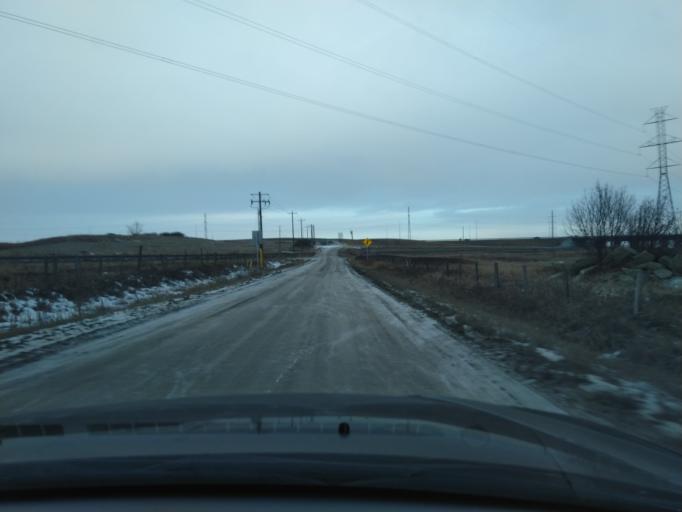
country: CA
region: Alberta
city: Airdrie
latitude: 51.1716
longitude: -114.0249
